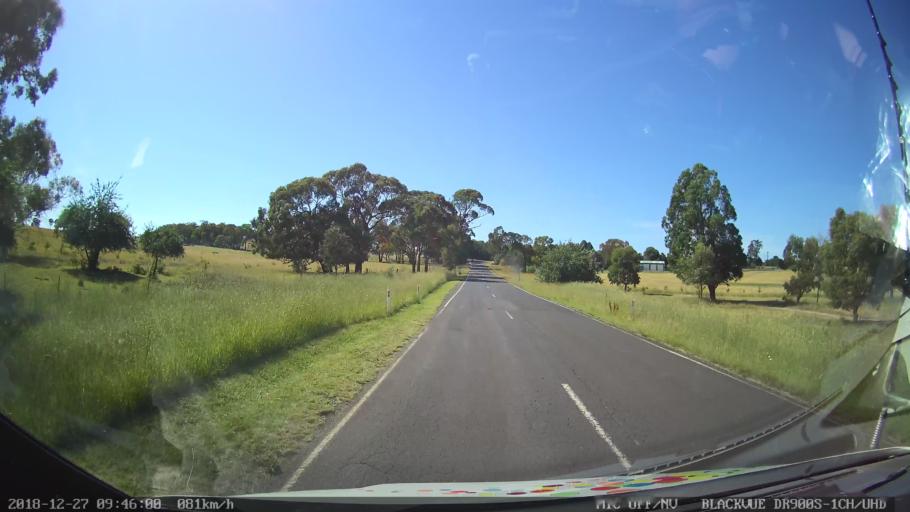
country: AU
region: New South Wales
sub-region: Lithgow
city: Portland
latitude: -33.3310
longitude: 149.9841
